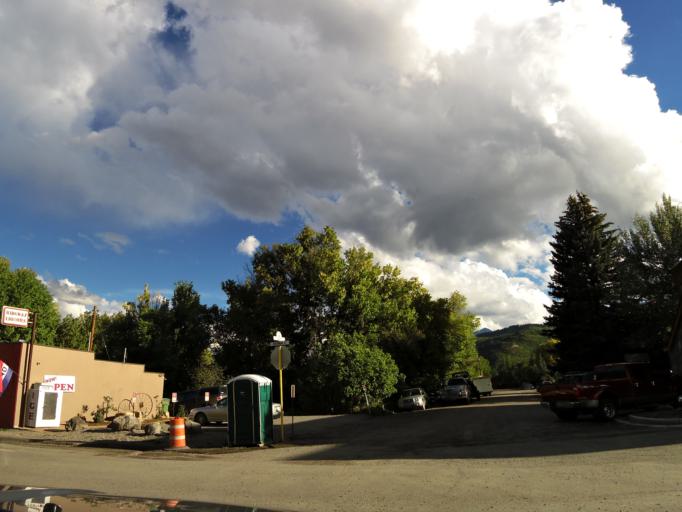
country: US
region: Colorado
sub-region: Ouray County
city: Ouray
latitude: 38.1515
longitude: -107.7577
